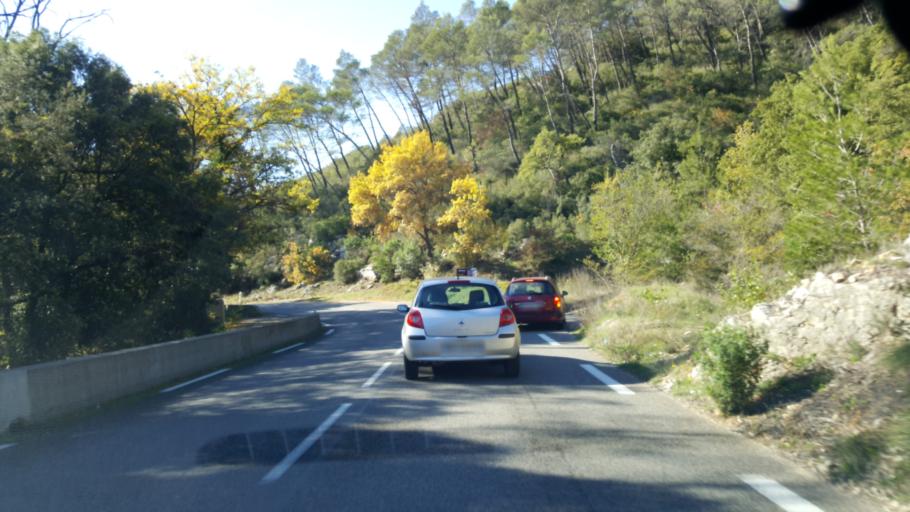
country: FR
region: Provence-Alpes-Cote d'Azur
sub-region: Departement du Var
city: Saint-Zacharie
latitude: 43.3851
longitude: 5.7346
